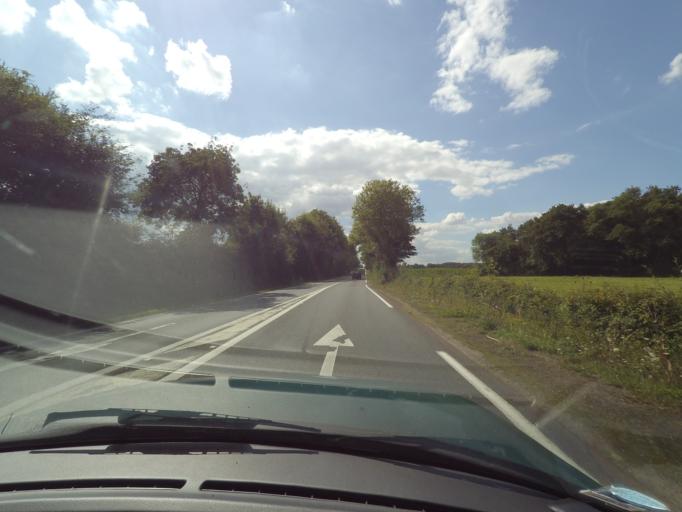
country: FR
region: Pays de la Loire
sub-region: Departement de la Vendee
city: La Guyonniere
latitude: 46.9826
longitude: -1.2714
